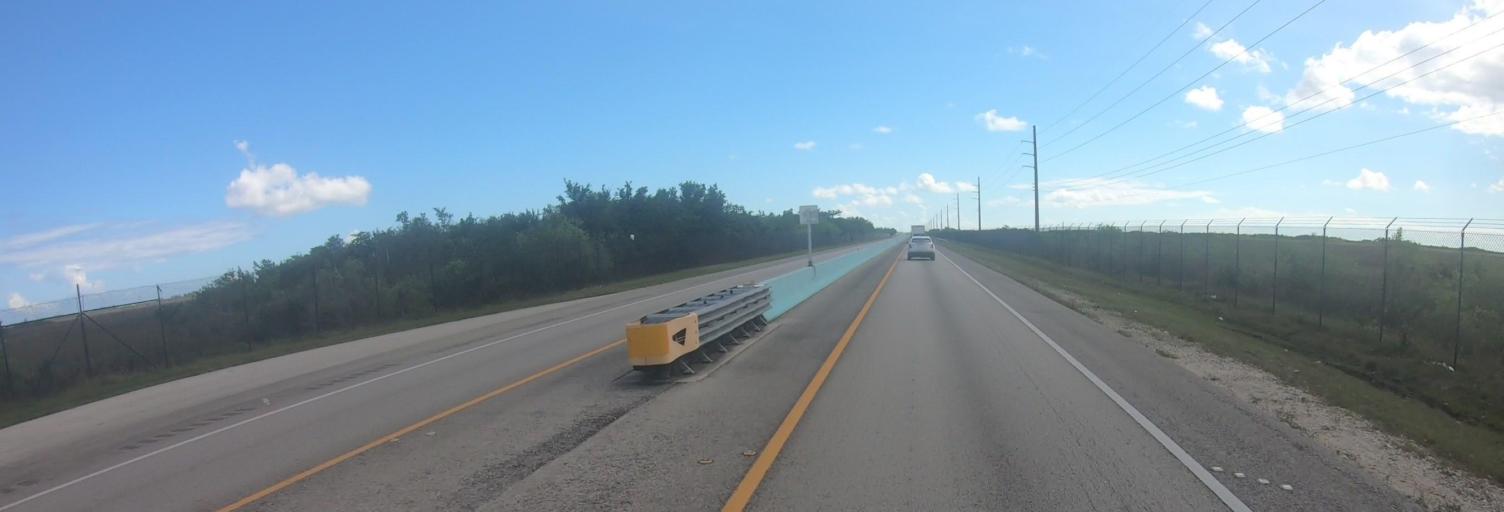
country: US
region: Florida
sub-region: Miami-Dade County
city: Florida City
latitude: 25.3377
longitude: -80.4553
